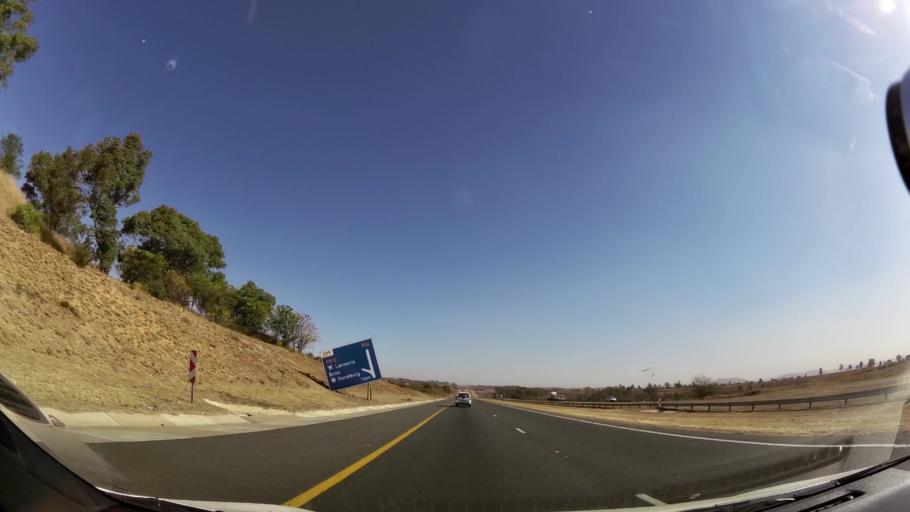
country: ZA
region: Gauteng
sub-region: City of Johannesburg Metropolitan Municipality
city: Diepsloot
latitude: -25.9748
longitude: 27.9384
